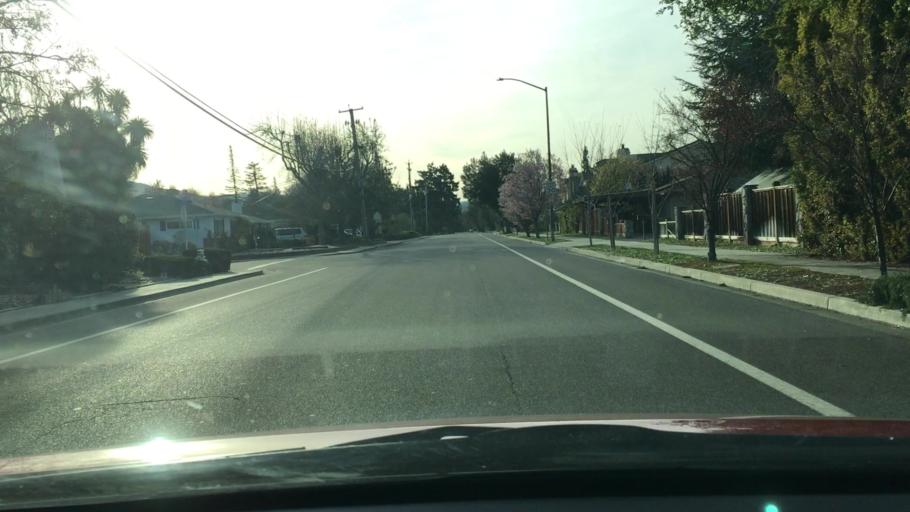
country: US
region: California
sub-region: Santa Clara County
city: Mountain View
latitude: 37.3613
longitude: -122.0714
